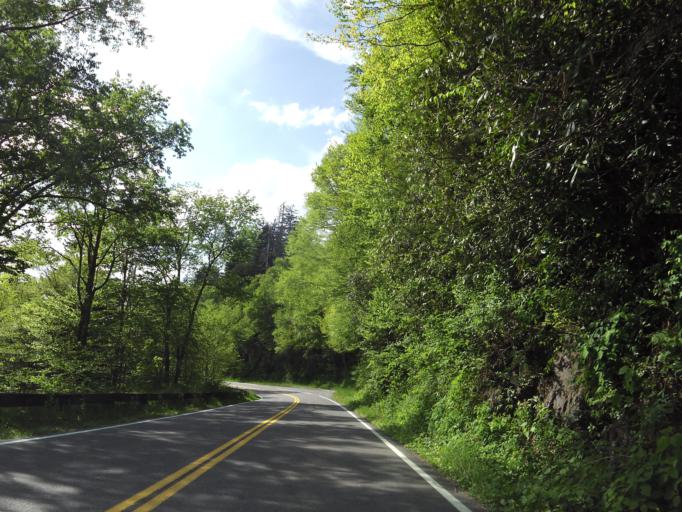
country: US
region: Tennessee
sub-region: Sevier County
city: Gatlinburg
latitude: 35.6143
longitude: -83.4228
